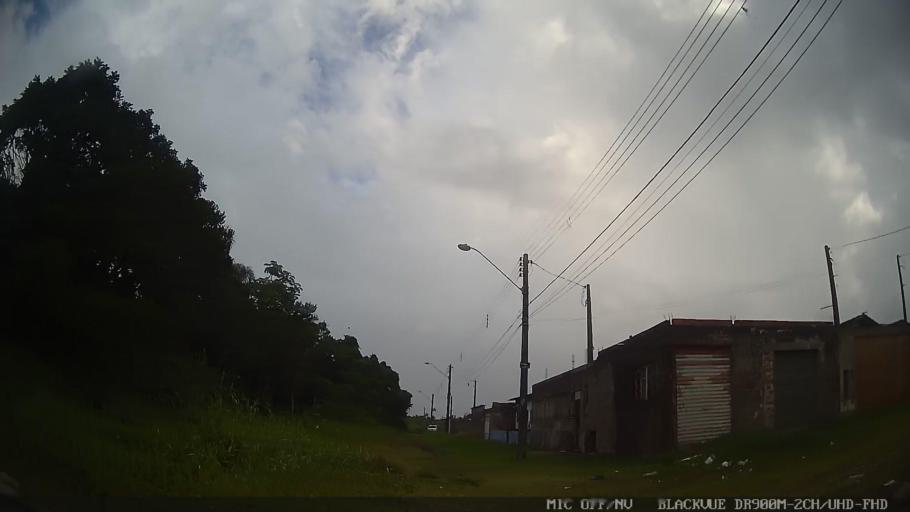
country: BR
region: Sao Paulo
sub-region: Itanhaem
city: Itanhaem
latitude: -24.2141
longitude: -46.8583
